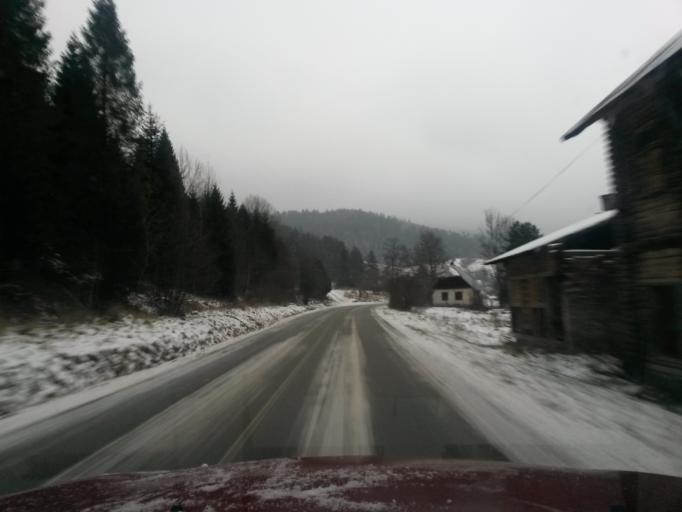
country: SK
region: Kosicky
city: Medzev
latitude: 48.7250
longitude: 20.7158
